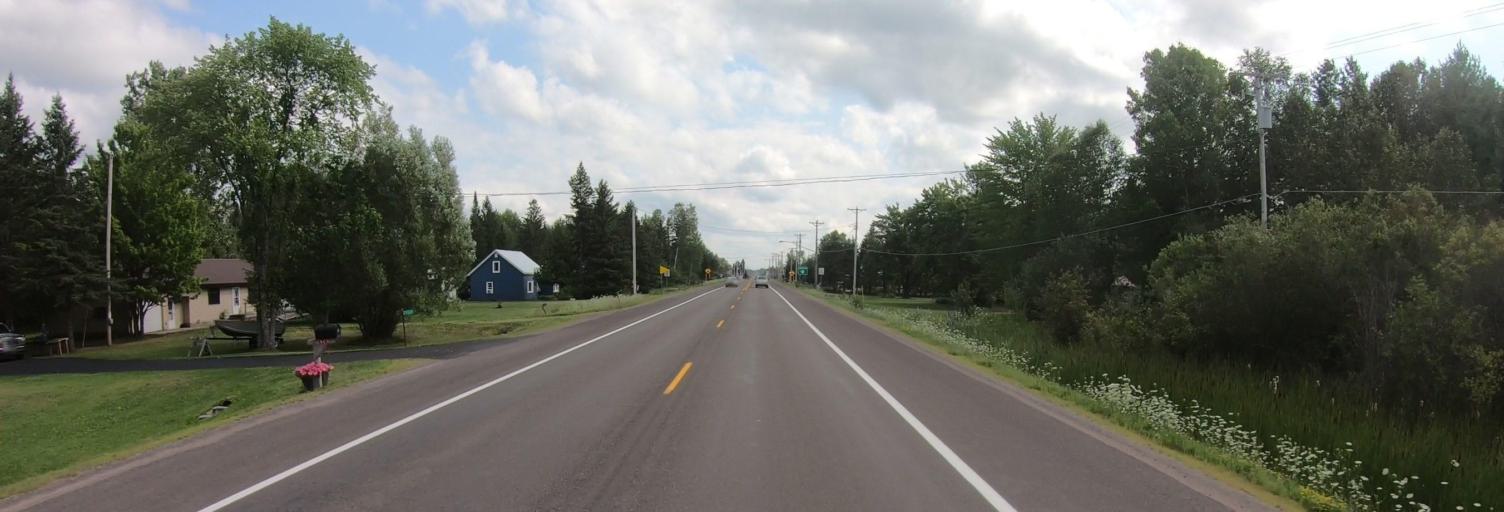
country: US
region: Michigan
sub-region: Ontonagon County
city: Ontonagon
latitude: 46.5397
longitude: -89.1786
